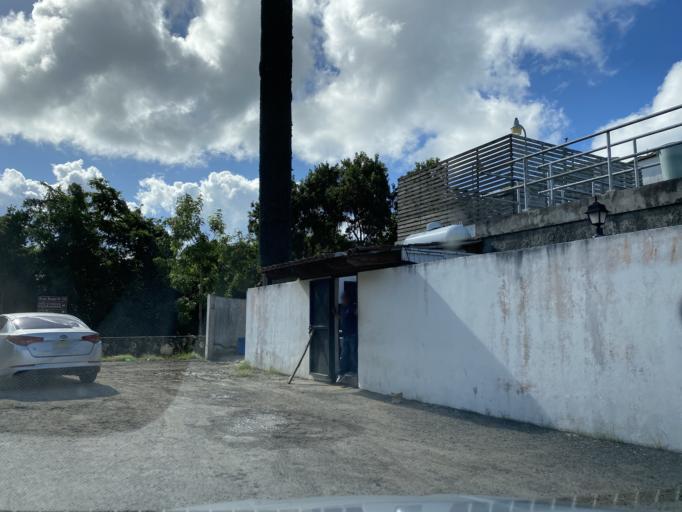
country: DO
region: La Altagracia
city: San Rafael del Yuma
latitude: 18.3334
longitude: -68.8082
